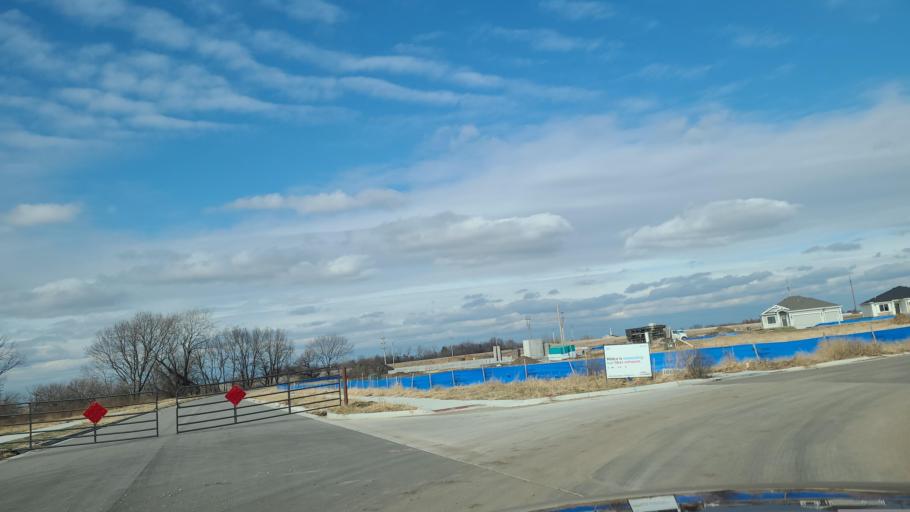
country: US
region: Kansas
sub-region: Douglas County
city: Eudora
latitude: 38.9187
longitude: -95.1015
